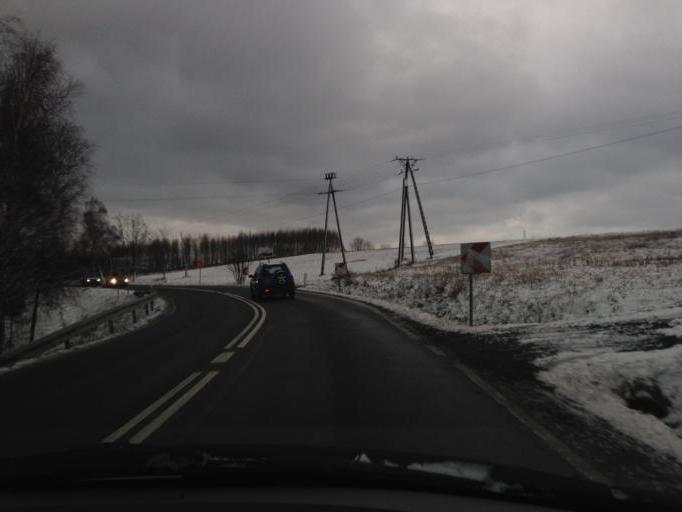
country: PL
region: Lesser Poland Voivodeship
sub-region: Powiat tarnowski
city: Gromnik
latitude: 49.8437
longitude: 20.9365
